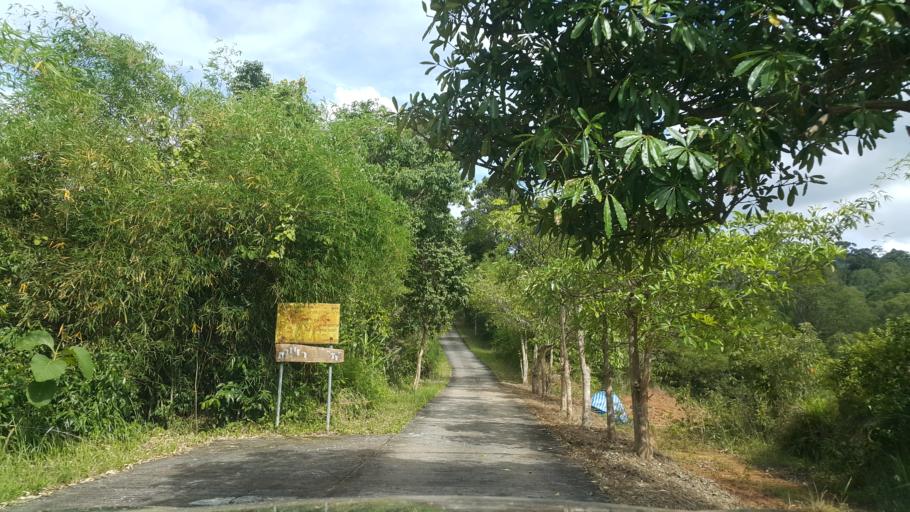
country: TH
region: Loei
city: Na Haeo
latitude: 17.5635
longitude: 100.9500
